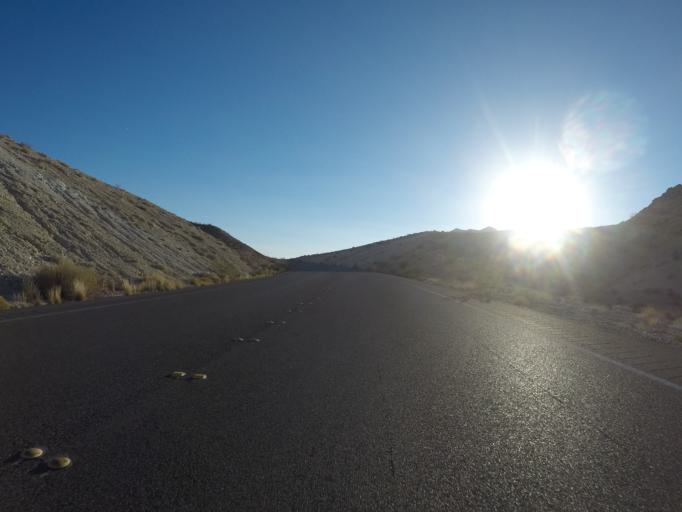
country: US
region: Nevada
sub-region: Clark County
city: Moapa Valley
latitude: 36.3605
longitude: -114.4831
